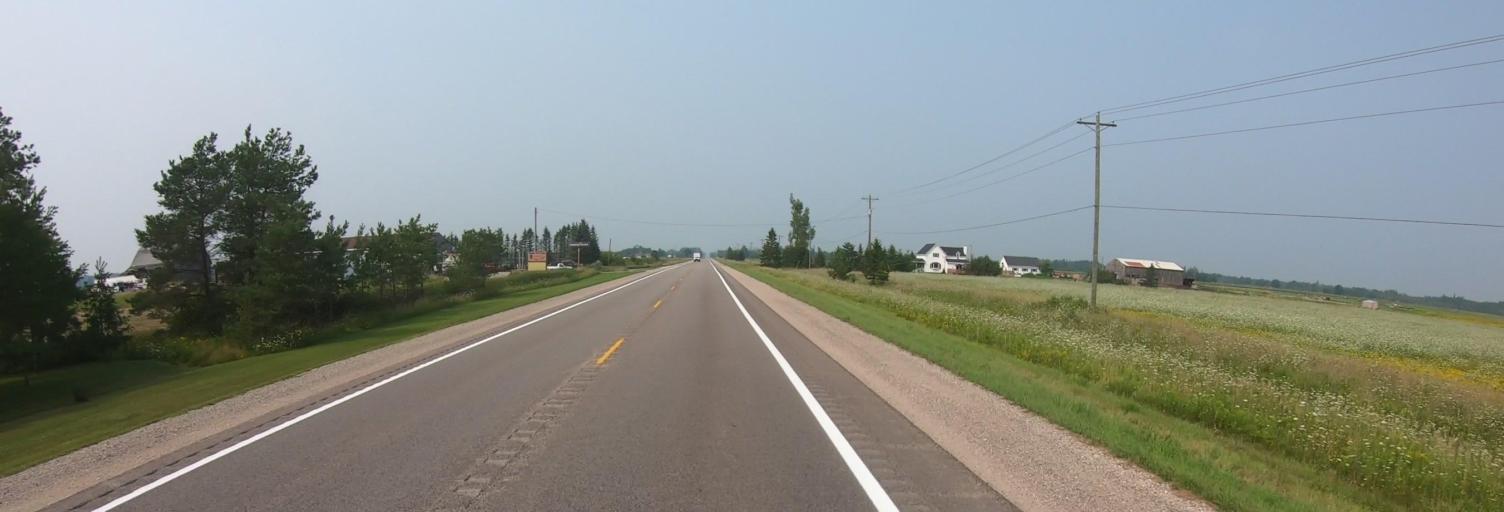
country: US
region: Michigan
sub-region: Chippewa County
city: Sault Ste. Marie
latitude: 46.1656
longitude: -84.3635
